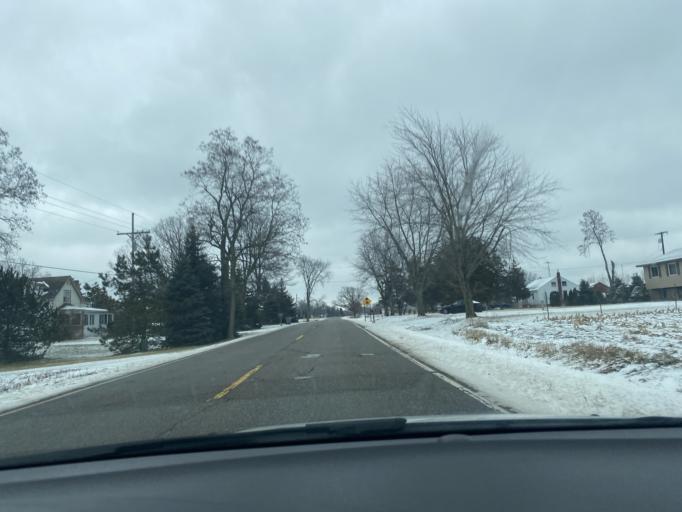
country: US
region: Michigan
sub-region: Lapeer County
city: Barnes Lake-Millers Lake
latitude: 43.2064
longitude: -83.2579
